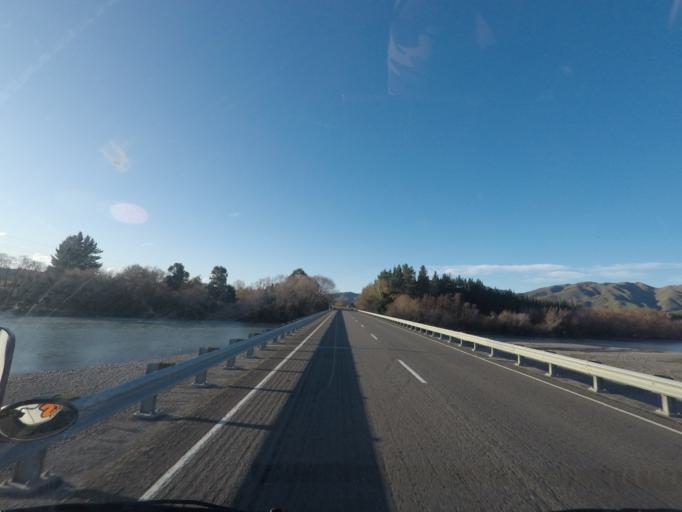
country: NZ
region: Canterbury
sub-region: Kaikoura District
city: Kaikoura
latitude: -42.7208
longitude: 173.2848
